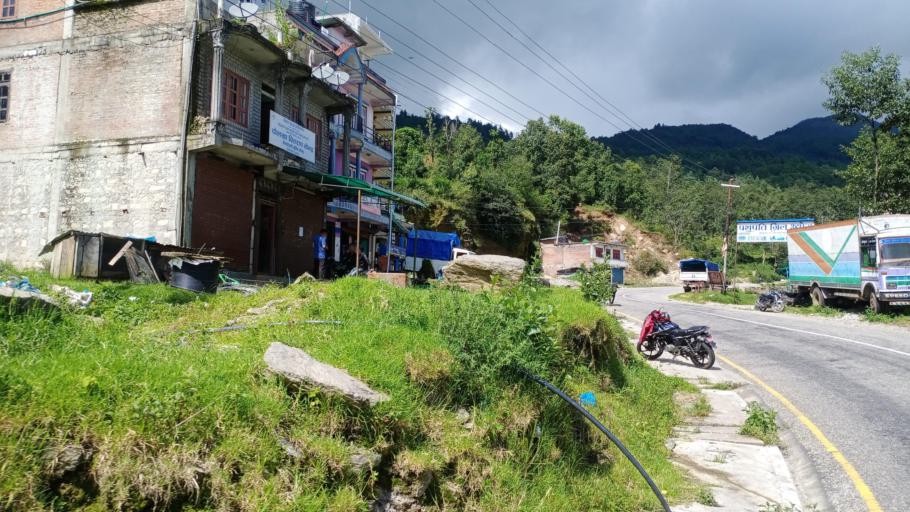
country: NP
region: Central Region
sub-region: Janakpur Zone
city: Ramechhap
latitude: 27.6487
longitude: 86.1397
